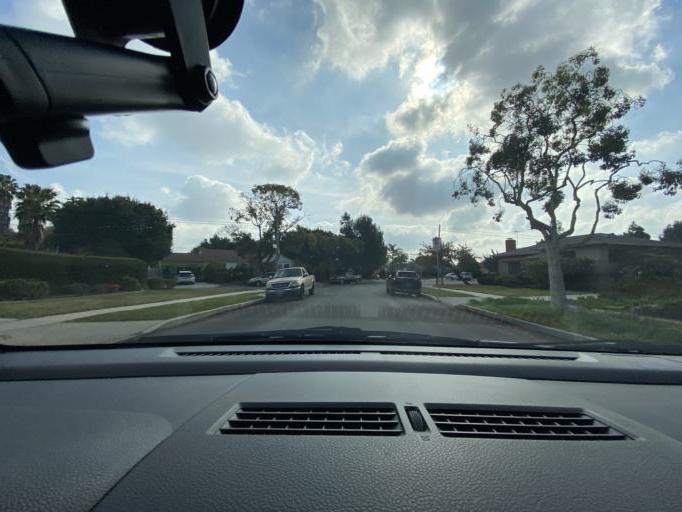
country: US
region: California
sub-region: Los Angeles County
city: Culver City
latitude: 34.0111
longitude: -118.4253
